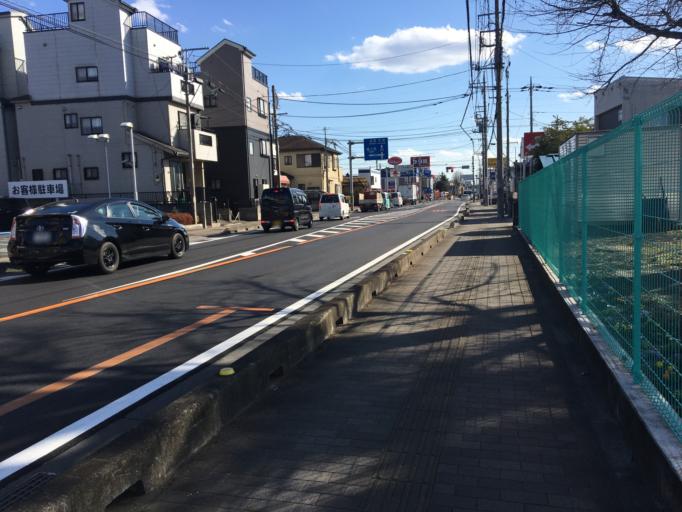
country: JP
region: Saitama
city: Oi
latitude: 35.8549
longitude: 139.5153
